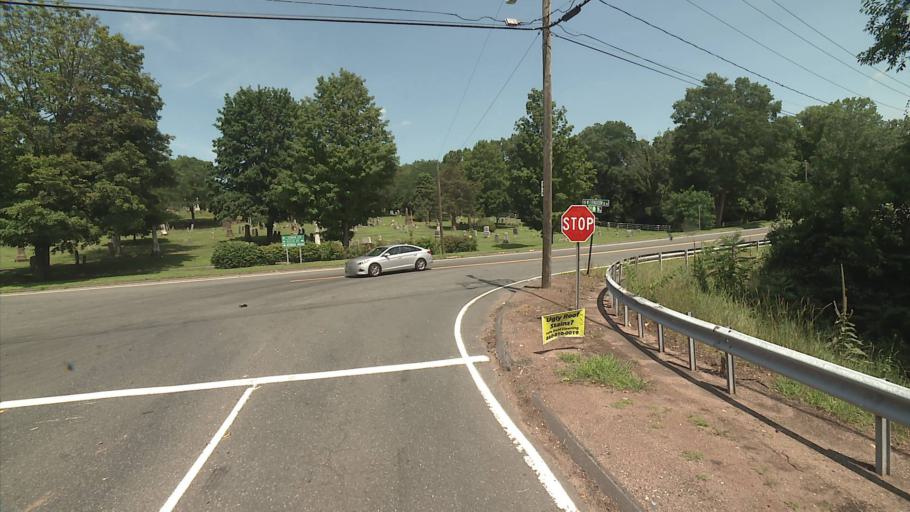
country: US
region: Connecticut
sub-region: Tolland County
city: Rockville
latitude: 41.8363
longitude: -72.4628
